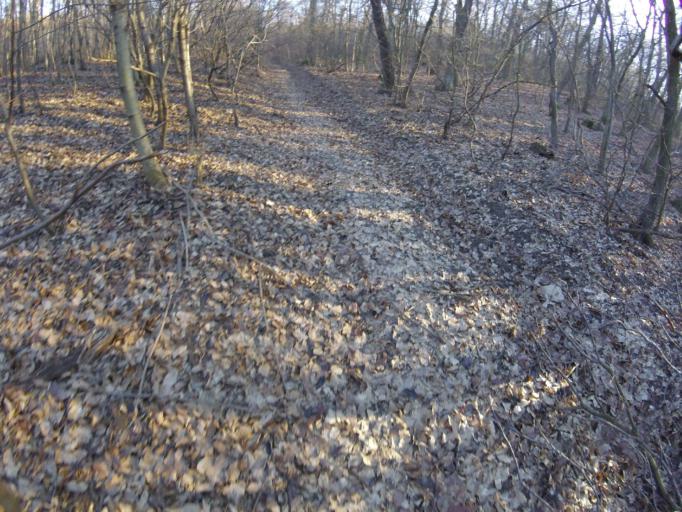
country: HU
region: Pest
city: Budakeszi
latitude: 47.4953
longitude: 18.9496
